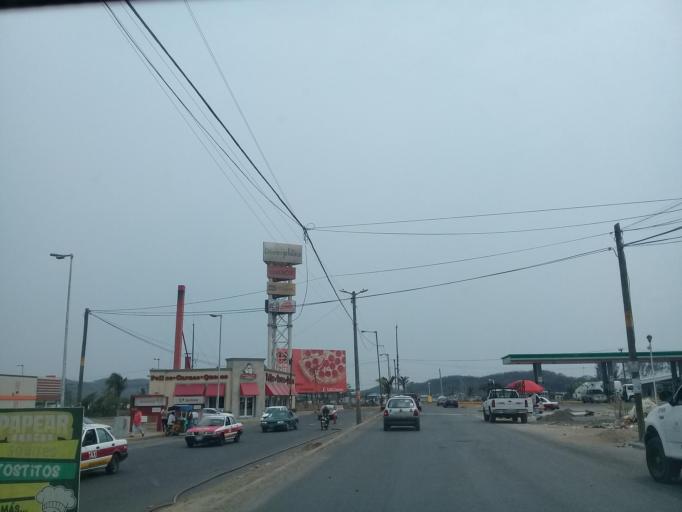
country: MX
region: Veracruz
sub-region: Veracruz
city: Rio Medio [Granja]
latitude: 19.2128
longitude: -96.2002
